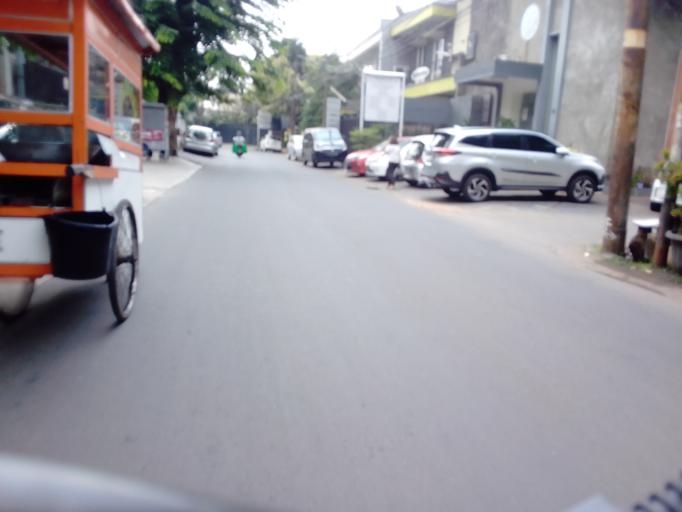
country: ID
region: Jakarta Raya
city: Jakarta
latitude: -6.2126
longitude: 106.8111
